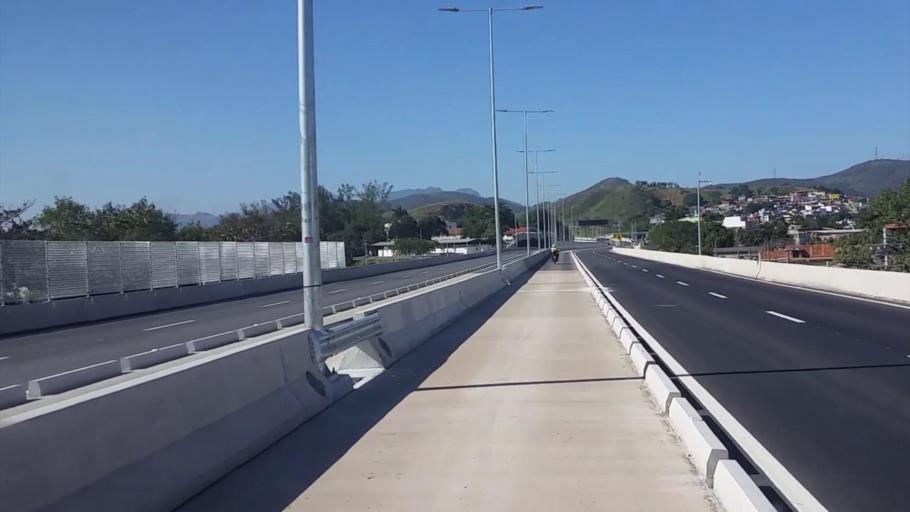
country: BR
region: Rio de Janeiro
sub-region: Nilopolis
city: Nilopolis
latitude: -22.8722
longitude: -43.4087
